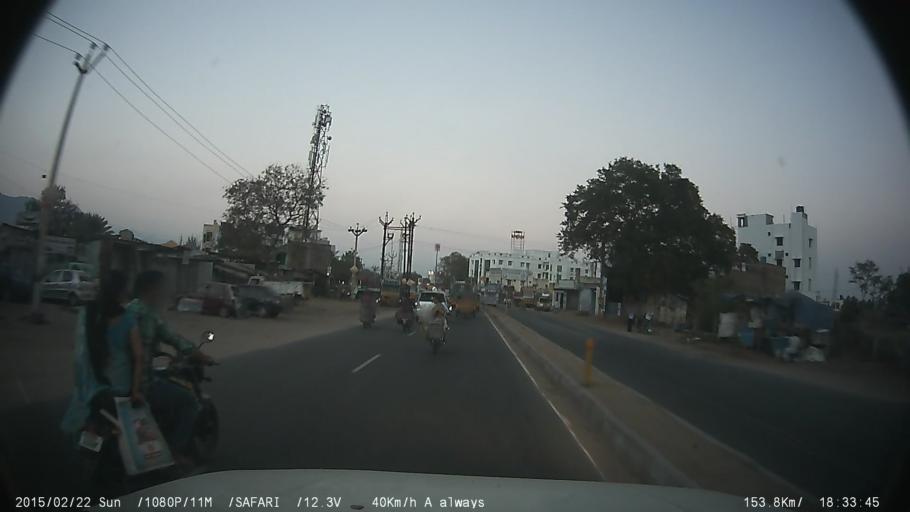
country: IN
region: Tamil Nadu
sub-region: Theni
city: Teni
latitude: 10.0051
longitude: 77.4713
